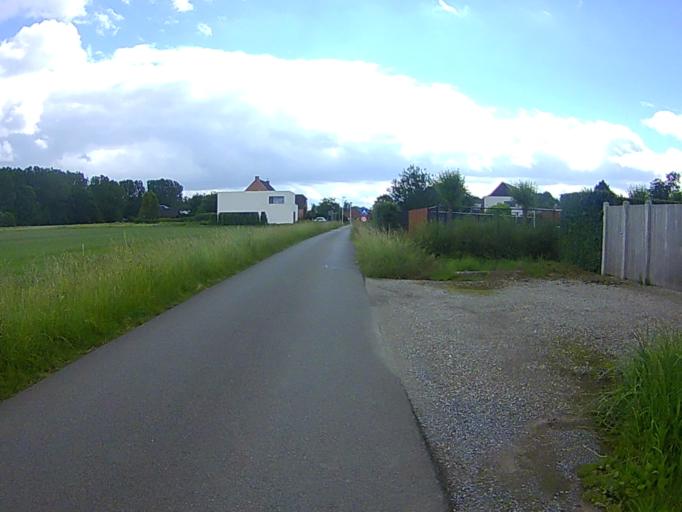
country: BE
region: Flanders
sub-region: Provincie Antwerpen
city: Lier
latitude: 51.1593
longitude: 4.5799
